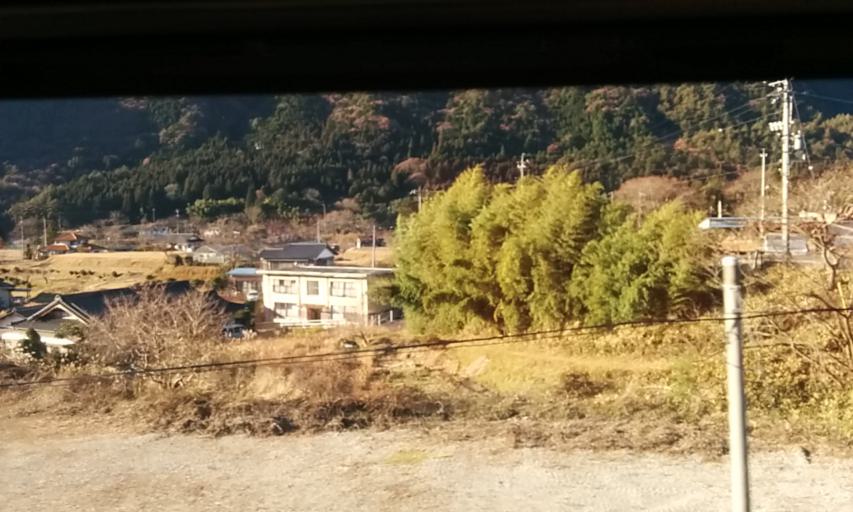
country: JP
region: Gifu
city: Nakatsugawa
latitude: 35.6715
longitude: 137.6341
